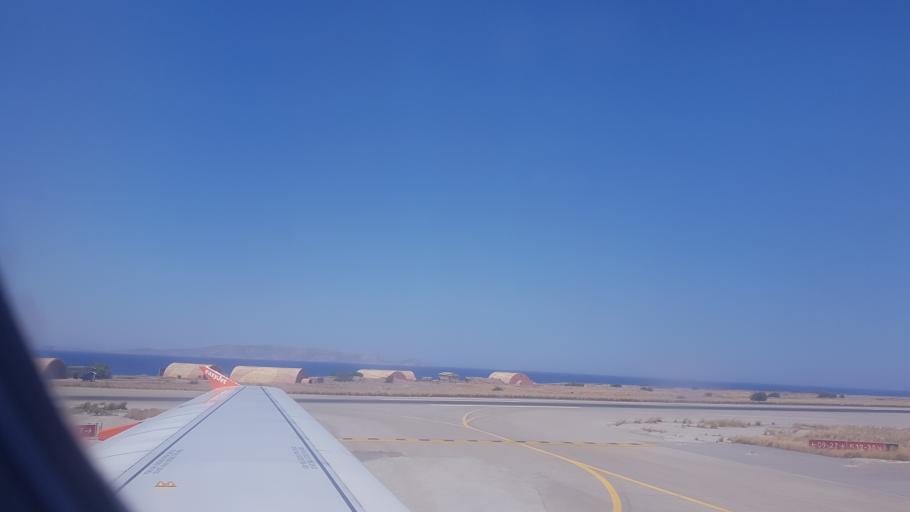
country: GR
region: Crete
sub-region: Nomos Irakleiou
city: Nea Alikarnassos
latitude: 35.3387
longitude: 25.1796
